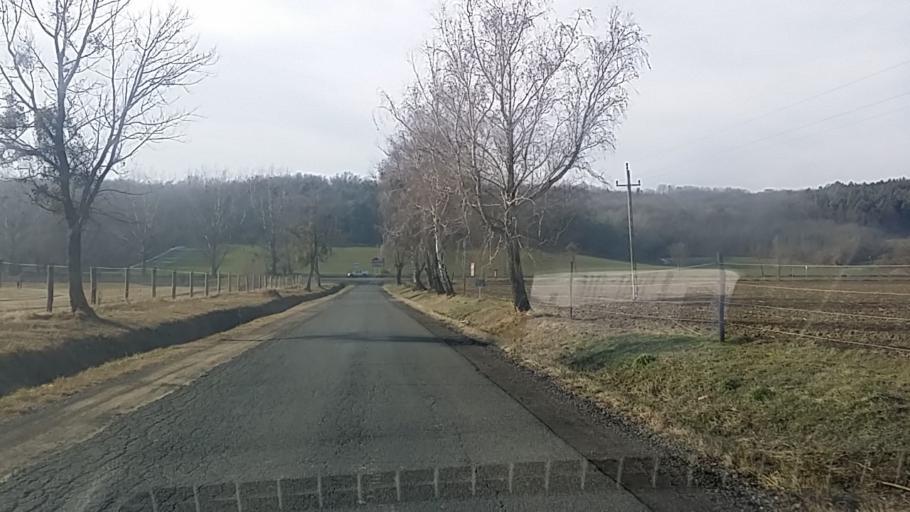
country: HU
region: Zala
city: Heviz
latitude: 46.8290
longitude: 17.0951
